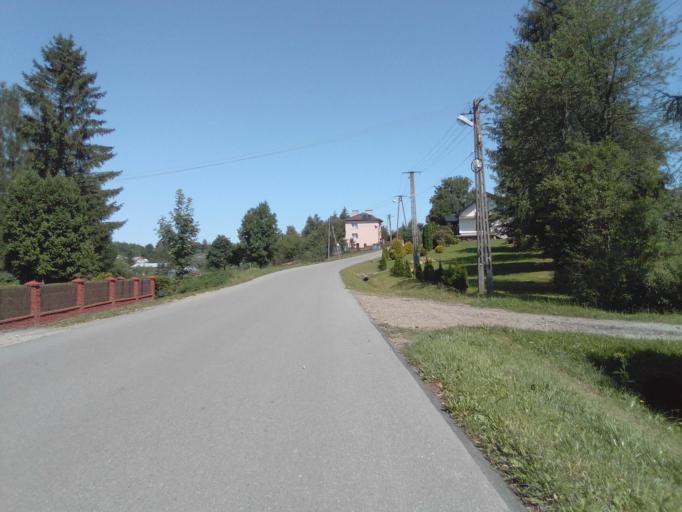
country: PL
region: Subcarpathian Voivodeship
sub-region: Powiat krosnienski
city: Chorkowka
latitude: 49.6516
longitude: 21.6080
